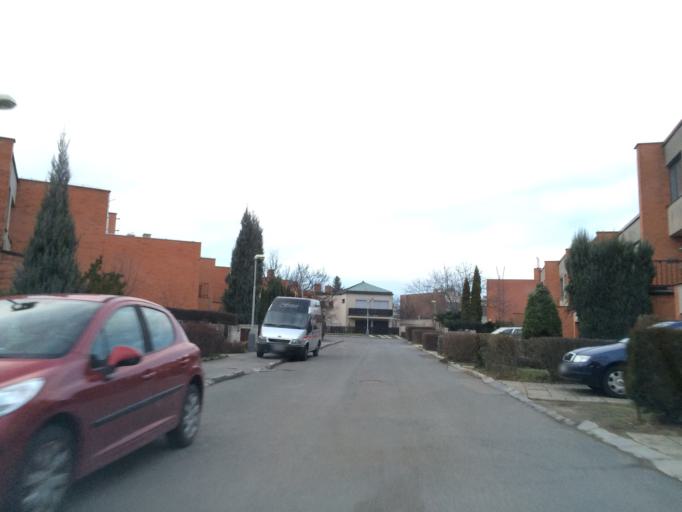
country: CZ
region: Praha
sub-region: Praha 1
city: Mala Strana
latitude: 50.1175
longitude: 14.3887
